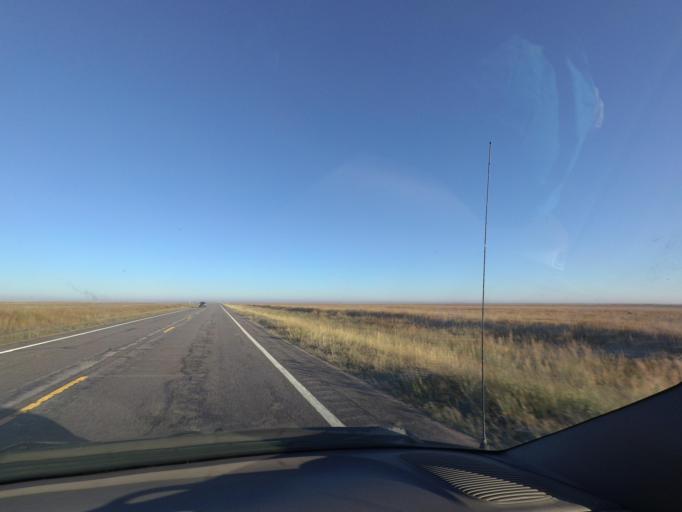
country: US
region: Colorado
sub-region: Washington County
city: Akron
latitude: 39.7076
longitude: -103.0779
